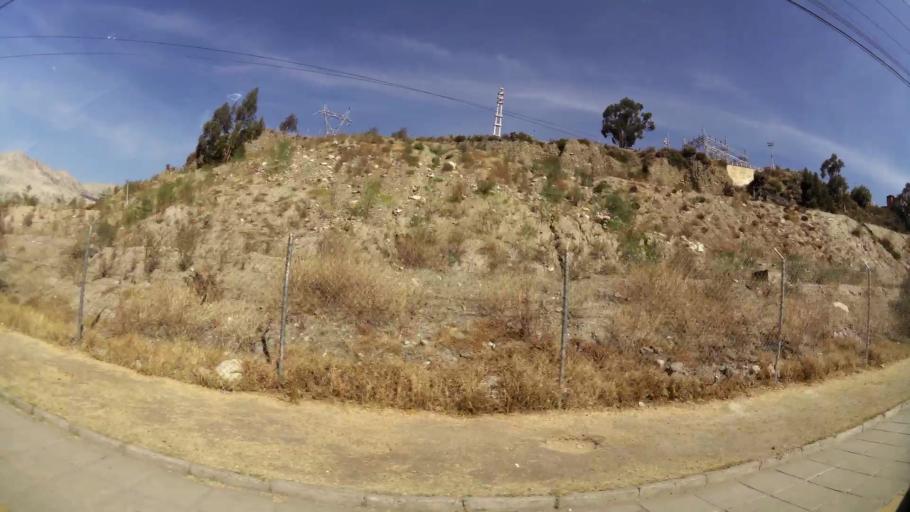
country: BO
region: La Paz
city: La Paz
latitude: -16.5170
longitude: -68.1148
